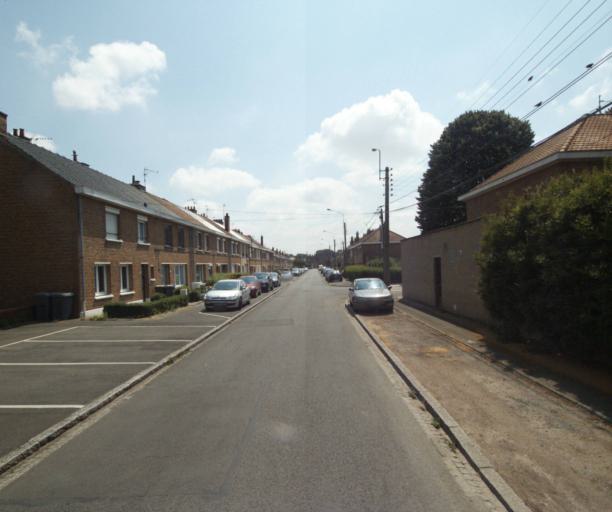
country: FR
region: Nord-Pas-de-Calais
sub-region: Departement du Nord
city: Armentieres
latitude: 50.6972
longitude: 2.8904
